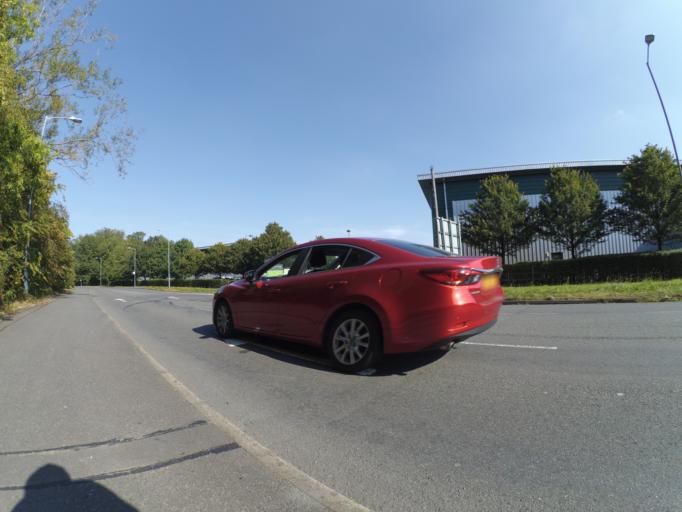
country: GB
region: England
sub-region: Warwickshire
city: Rugby
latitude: 52.3938
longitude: -1.2634
